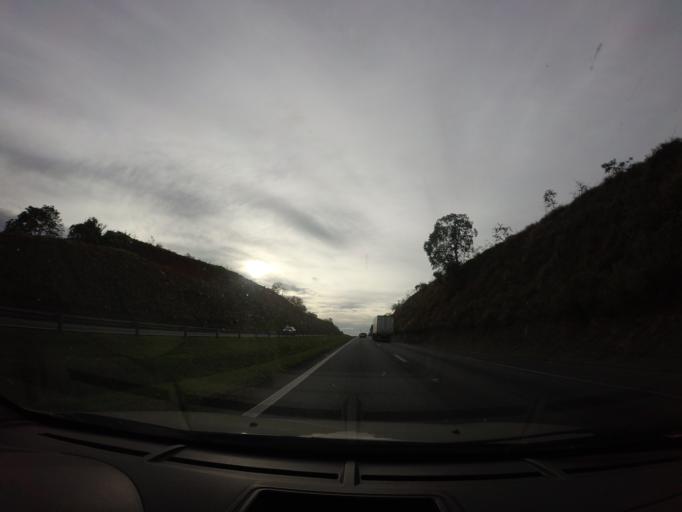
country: BR
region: Sao Paulo
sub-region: Itatiba
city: Itatiba
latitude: -22.9974
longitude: -46.7865
